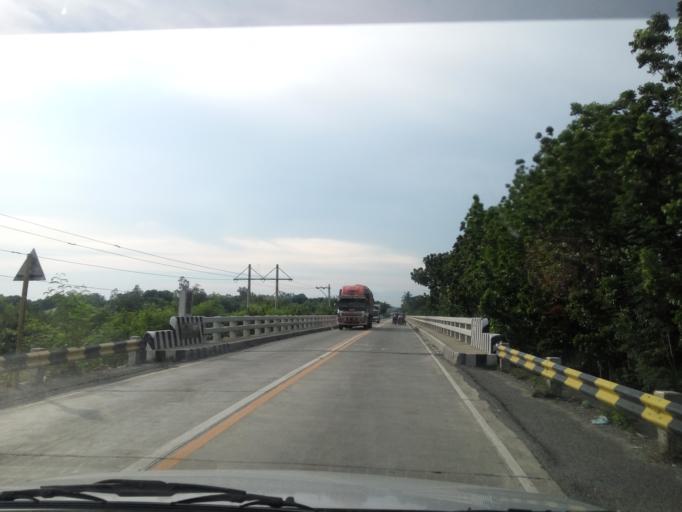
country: PH
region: Ilocos
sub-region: Province of Pangasinan
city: Binalonan
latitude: 16.0861
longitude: 120.5794
